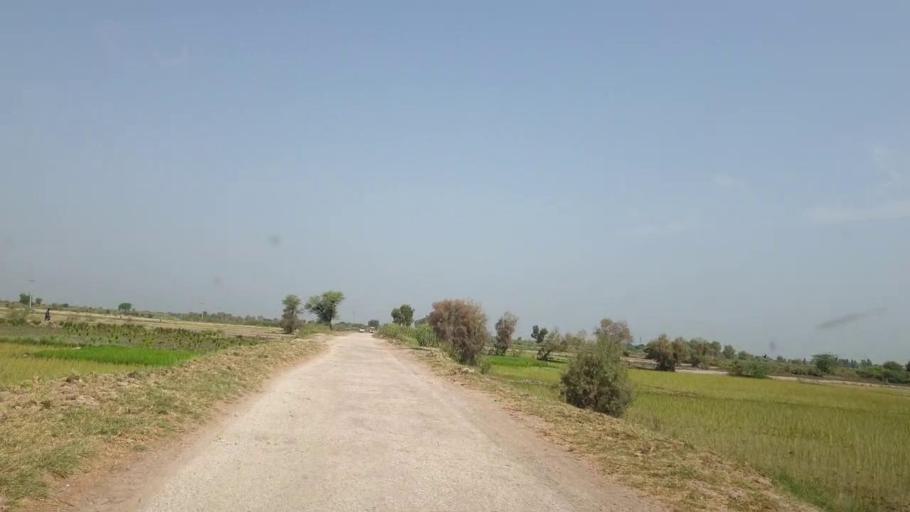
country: PK
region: Sindh
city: Lakhi
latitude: 27.8307
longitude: 68.6842
